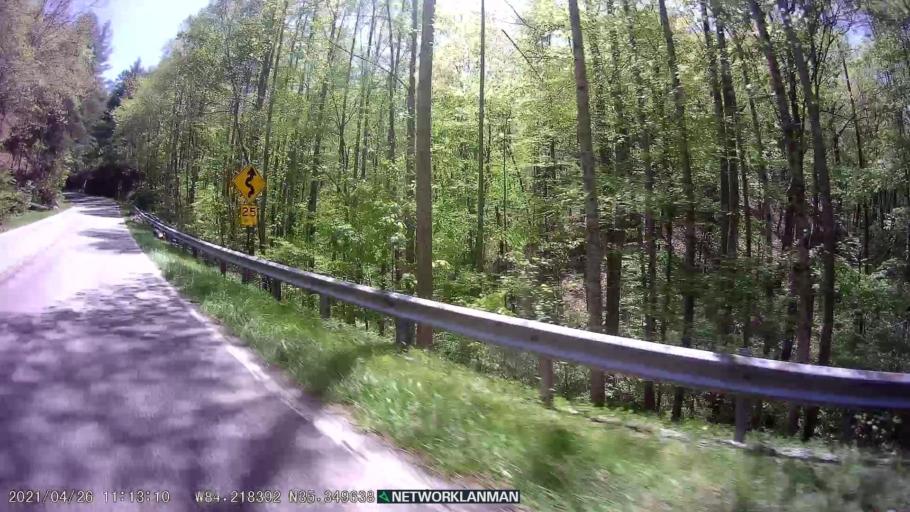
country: US
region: Tennessee
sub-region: Monroe County
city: Madisonville
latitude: 35.3496
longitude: -84.2184
